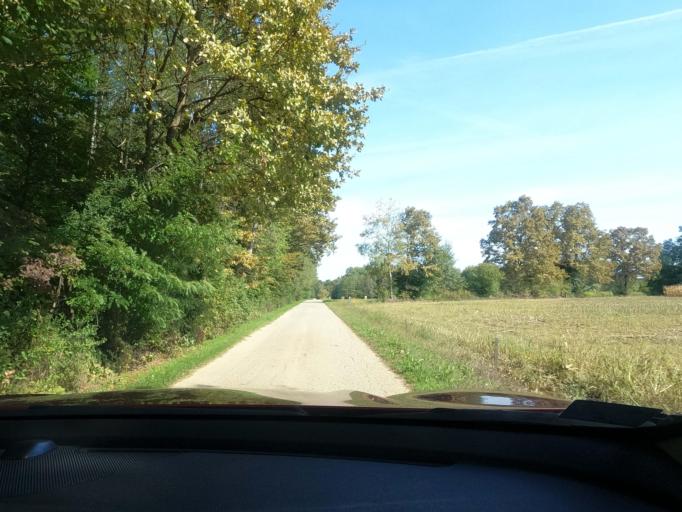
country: HR
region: Sisacko-Moslavacka
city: Petrinja
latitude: 45.3342
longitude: 16.2265
